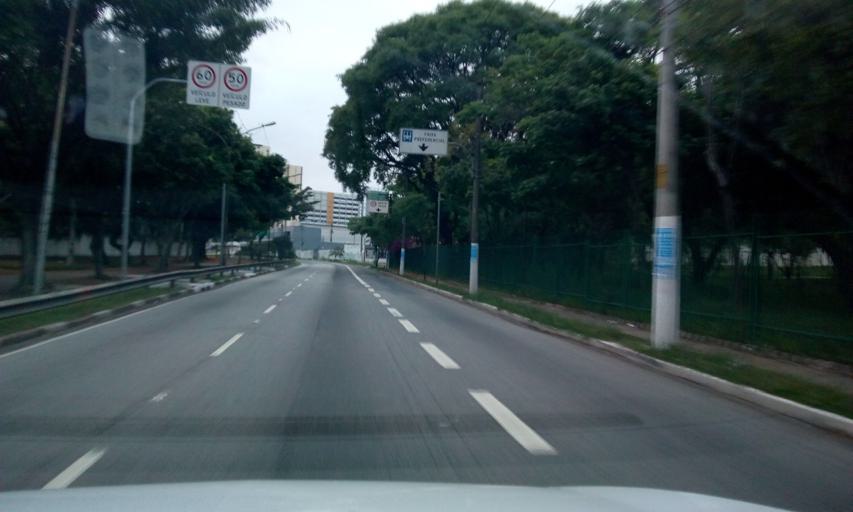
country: BR
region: Sao Paulo
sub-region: Sao Paulo
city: Sao Paulo
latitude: -23.5273
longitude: -46.5705
